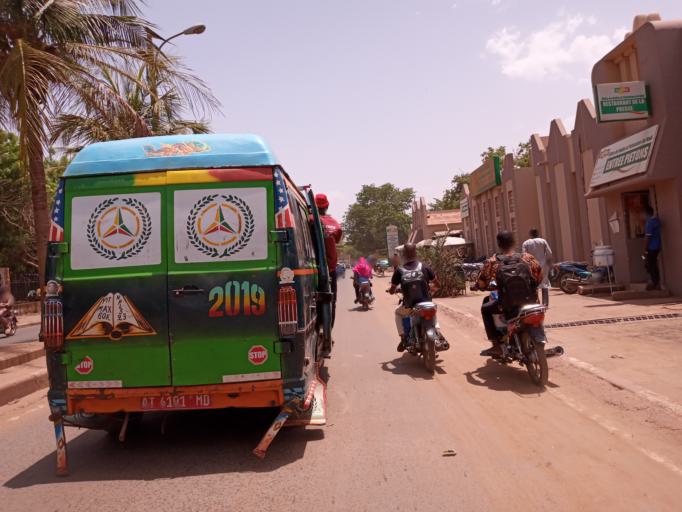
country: ML
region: Bamako
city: Bamako
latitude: 12.6396
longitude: -7.9934
